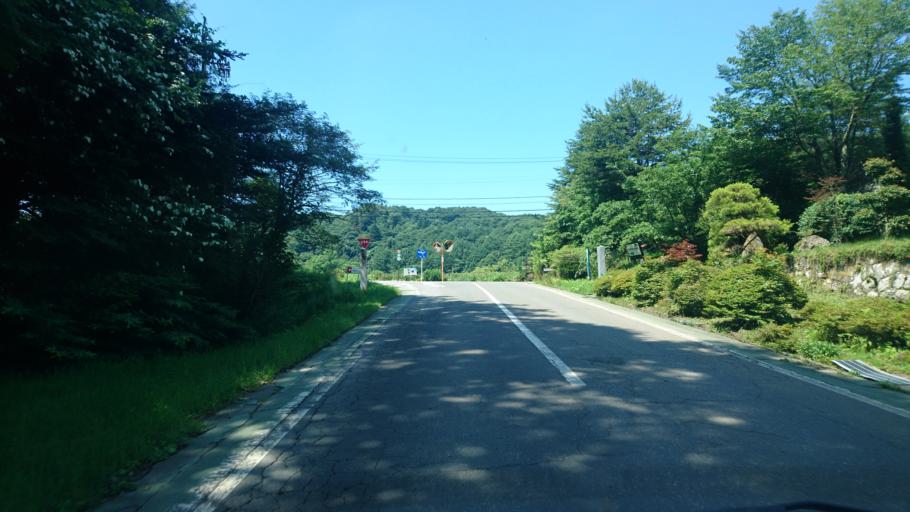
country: JP
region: Nagano
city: Saku
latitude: 36.3218
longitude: 138.5760
